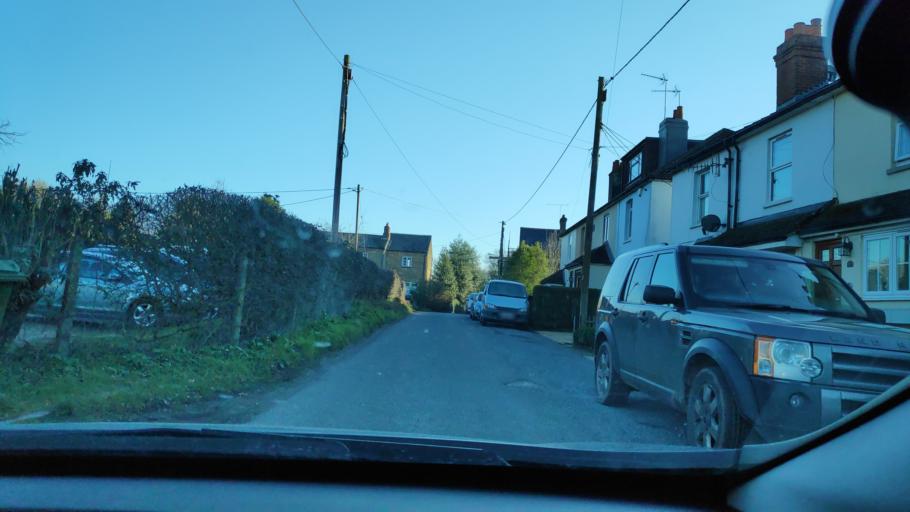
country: GB
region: England
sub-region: Surrey
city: Seale
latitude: 51.2510
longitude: -0.7059
